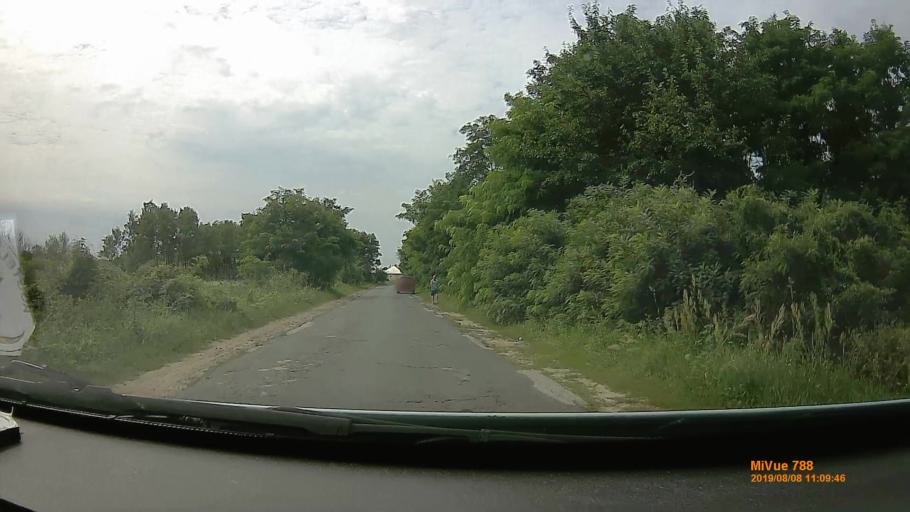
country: HU
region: Szabolcs-Szatmar-Bereg
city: Balkany
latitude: 47.7502
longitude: 21.8430
